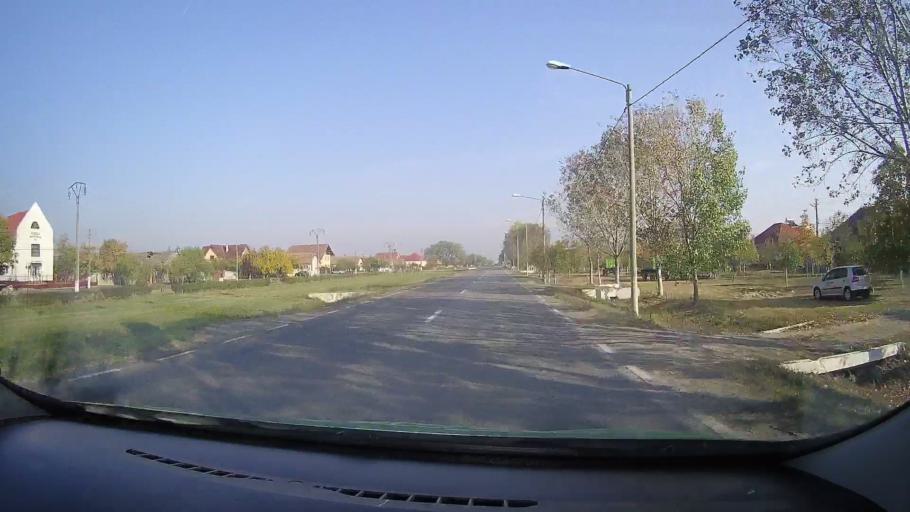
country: RO
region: Arad
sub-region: Comuna Pilu
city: Pilu
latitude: 46.5735
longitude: 21.3423
